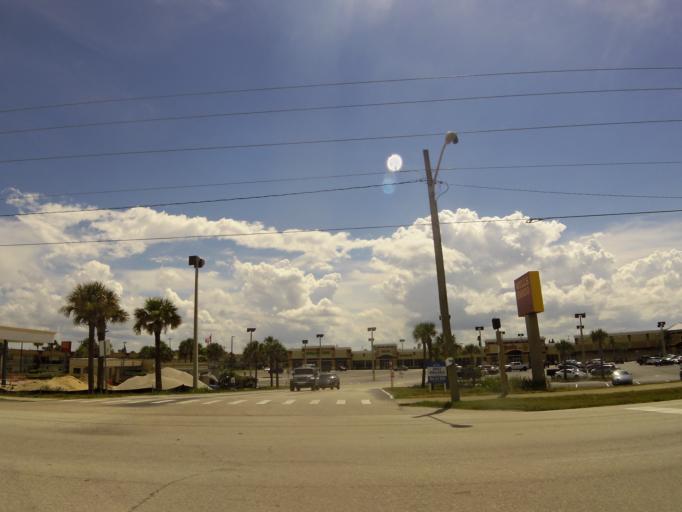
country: US
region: Florida
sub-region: Volusia County
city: Ormond-by-the-Sea
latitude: 29.3232
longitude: -81.0553
